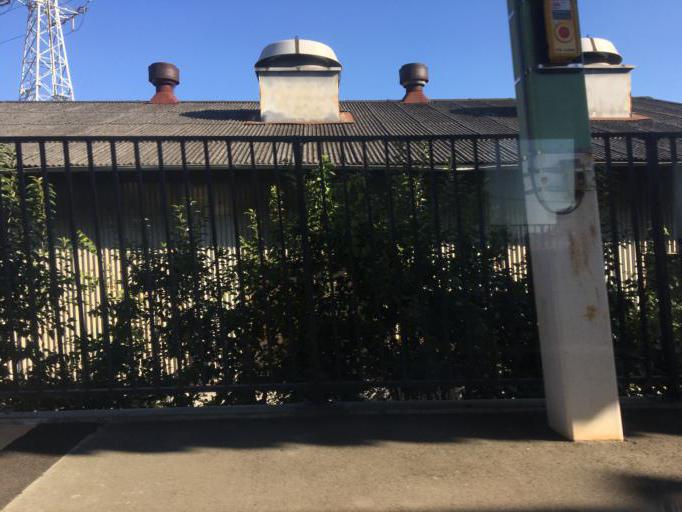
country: JP
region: Gunma
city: Maebashi-shi
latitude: 36.3709
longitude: 139.1092
